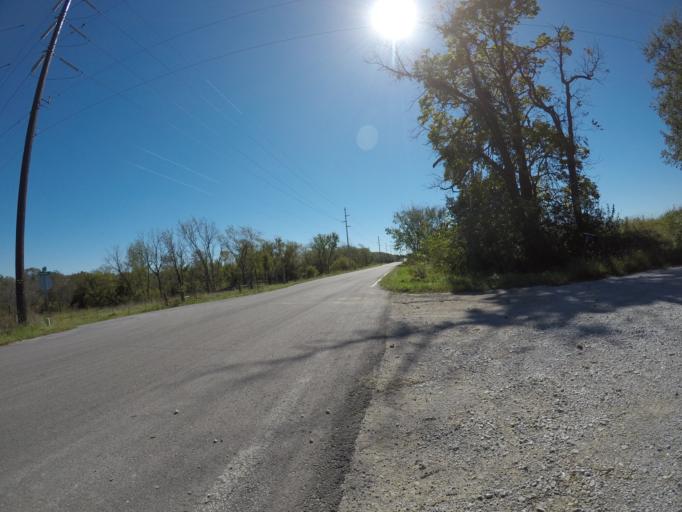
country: US
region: Kansas
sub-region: Johnson County
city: De Soto
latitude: 38.9568
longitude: -95.0195
